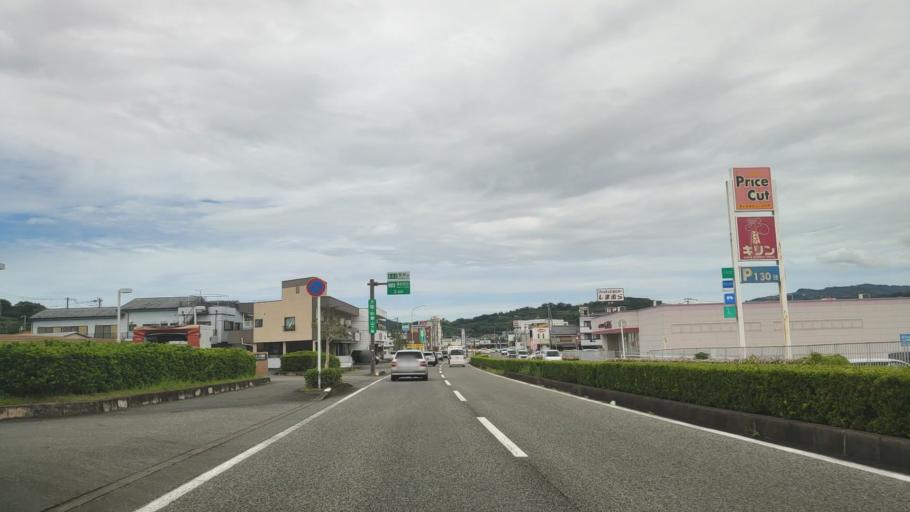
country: JP
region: Wakayama
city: Tanabe
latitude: 33.7383
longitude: 135.3952
